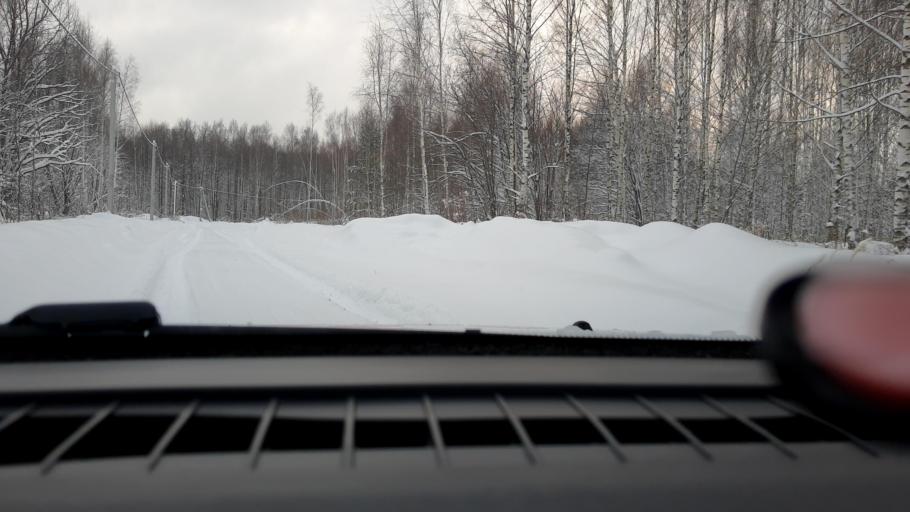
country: RU
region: Nizjnij Novgorod
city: Afonino
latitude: 56.1329
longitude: 43.9752
